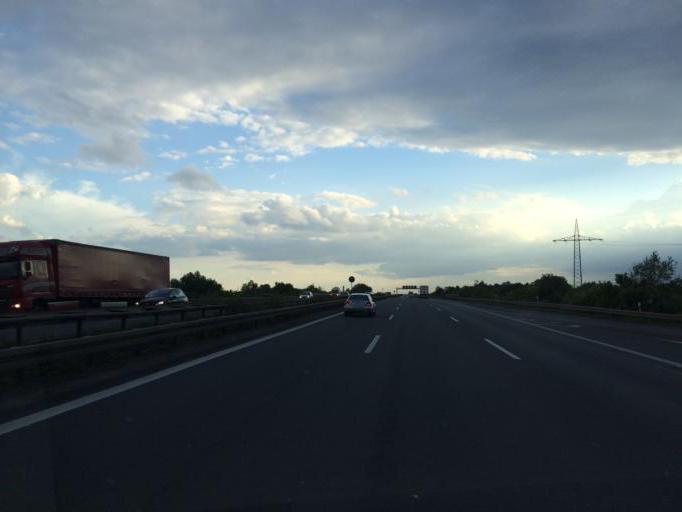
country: DE
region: Saxony-Anhalt
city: Glindenberg
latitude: 52.2130
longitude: 11.6677
